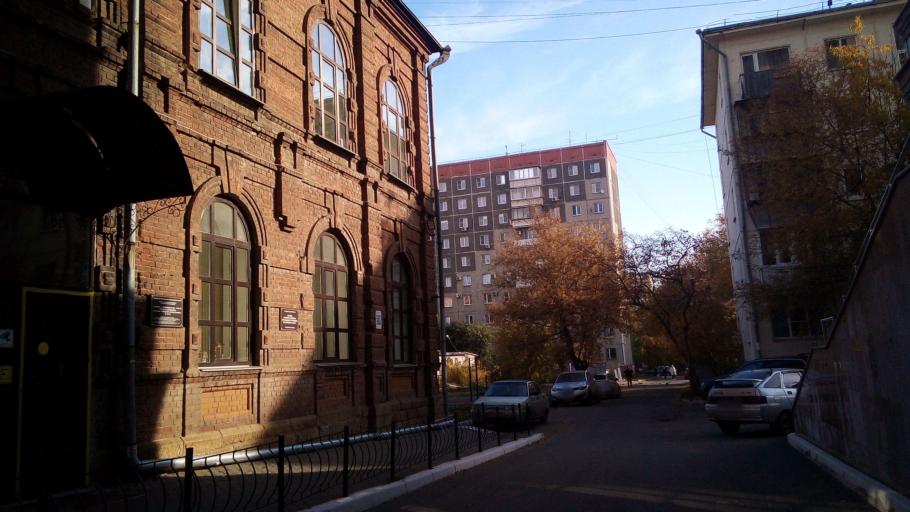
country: RU
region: Chelyabinsk
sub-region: Gorod Chelyabinsk
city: Chelyabinsk
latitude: 55.1519
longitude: 61.4118
